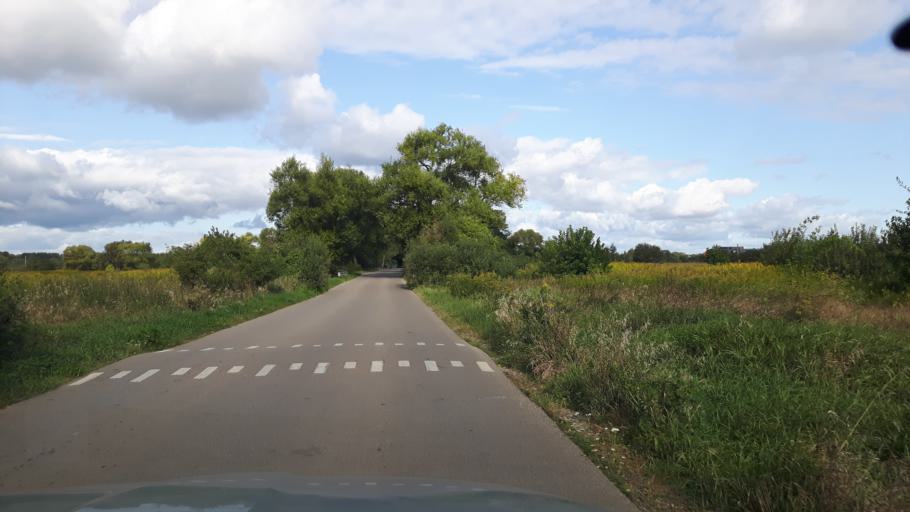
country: PL
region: Masovian Voivodeship
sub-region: Powiat wolominski
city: Marki
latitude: 52.3330
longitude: 21.0728
